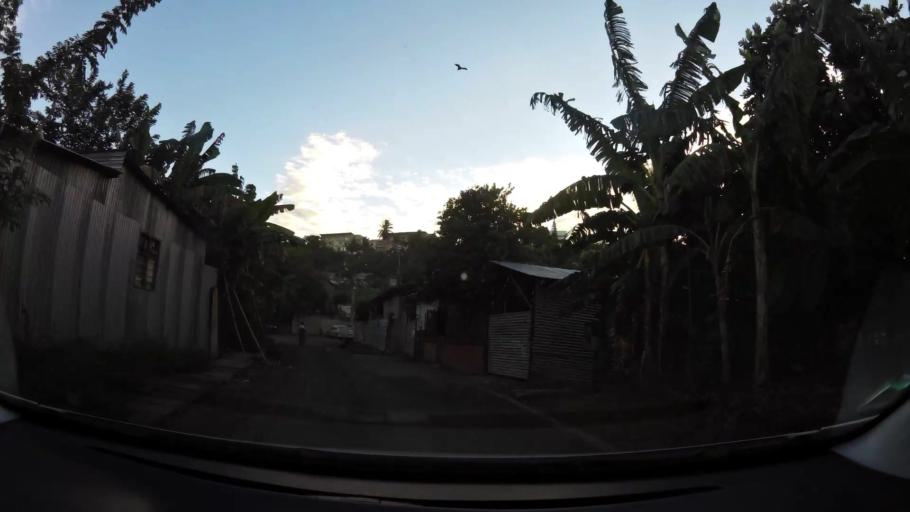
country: YT
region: Koungou
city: Koungou
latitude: -12.7323
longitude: 45.1993
